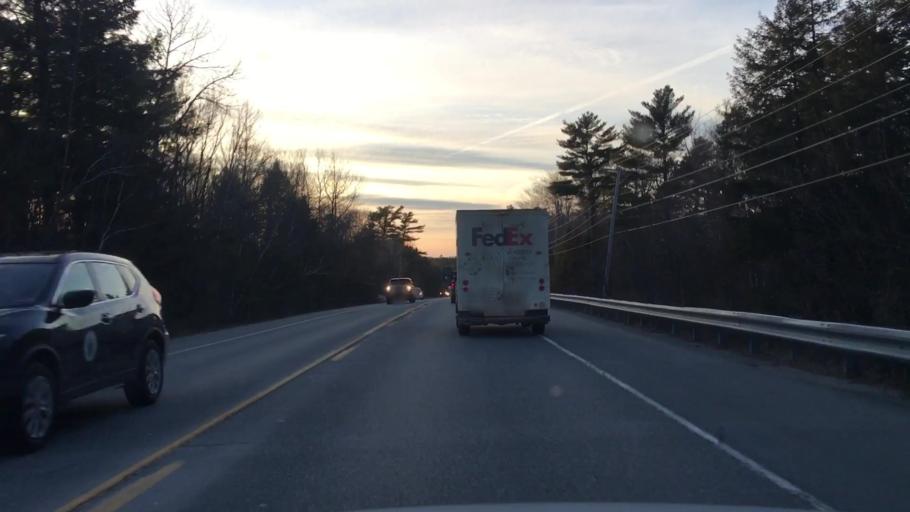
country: US
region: Maine
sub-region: Penobscot County
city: Holden
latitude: 44.7552
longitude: -68.6710
